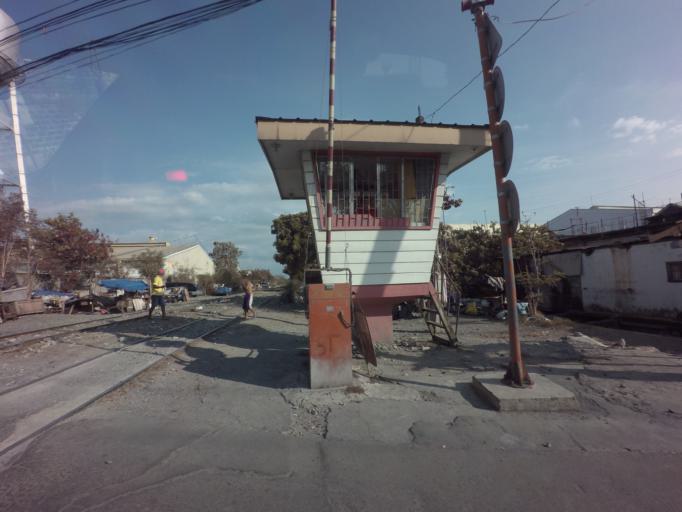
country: PH
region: Calabarzon
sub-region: Province of Rizal
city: Taguig
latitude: 14.4821
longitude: 121.0483
